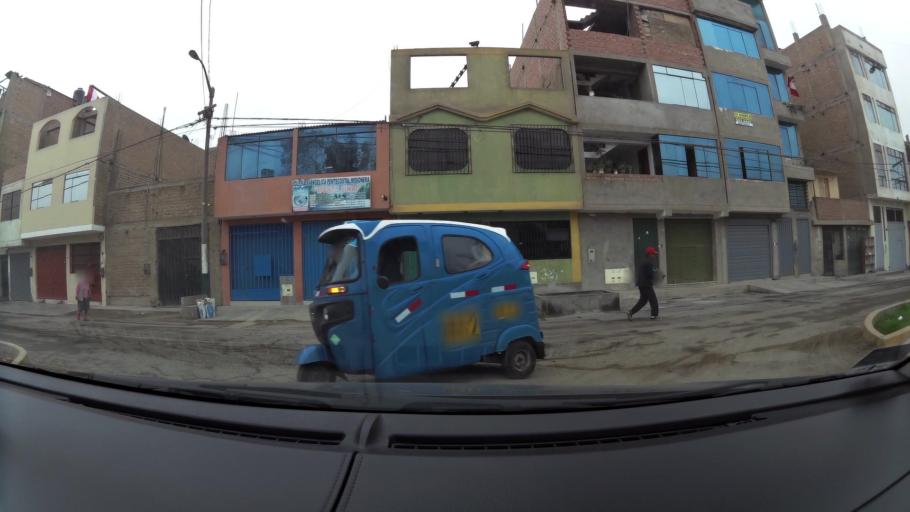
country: PE
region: Lima
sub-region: Lima
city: Independencia
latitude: -11.9700
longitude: -77.0817
